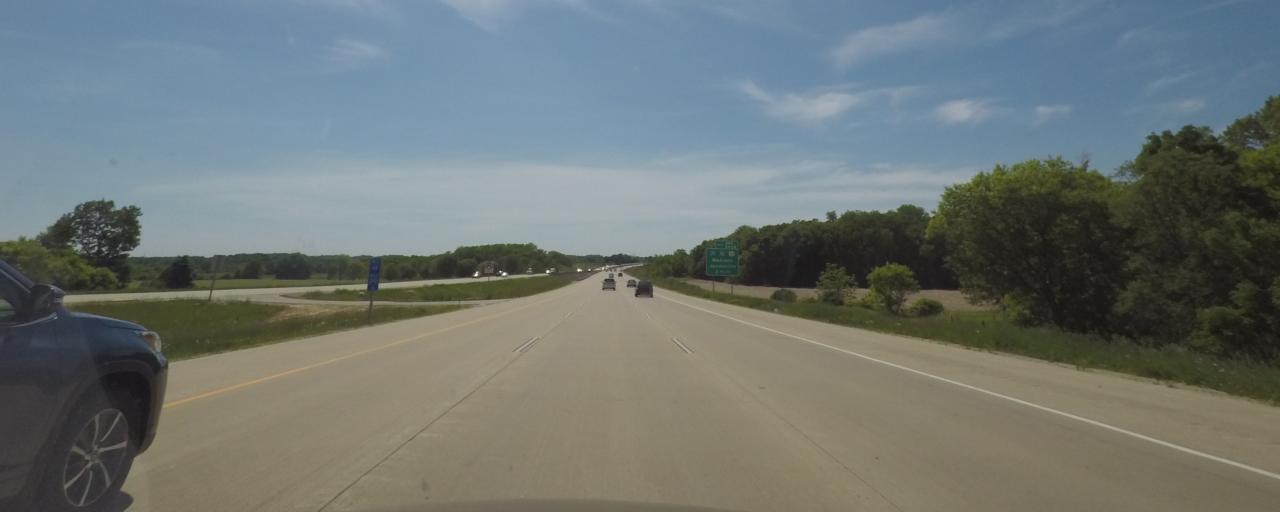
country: US
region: Wisconsin
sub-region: Dane County
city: Cottage Grove
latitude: 43.1067
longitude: -89.2386
